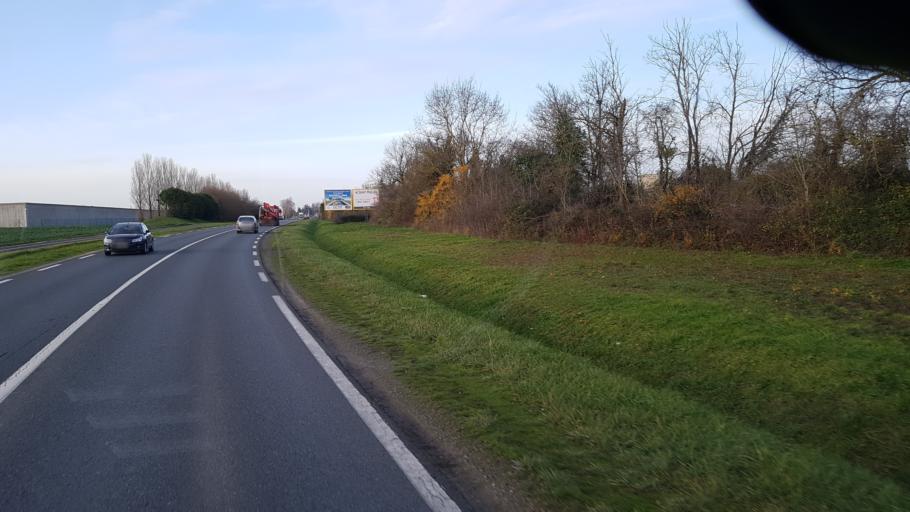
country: FR
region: Centre
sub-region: Departement de l'Indre
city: Chateauroux
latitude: 46.7960
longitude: 1.7250
